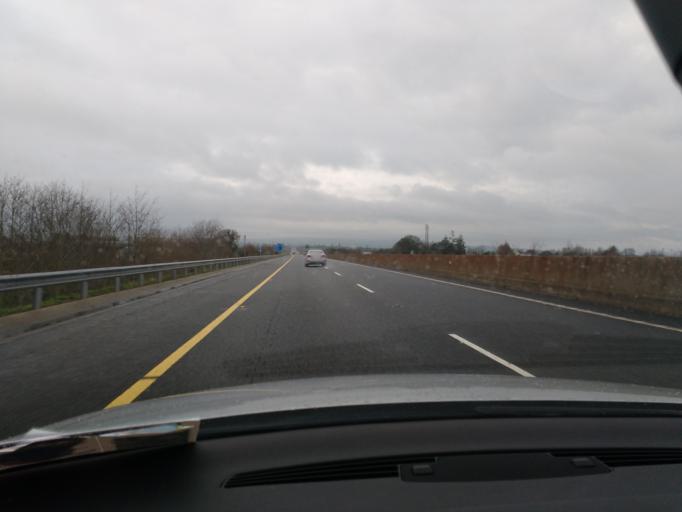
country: IE
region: Munster
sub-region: North Tipperary
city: Nenagh
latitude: 52.8492
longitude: -8.1624
